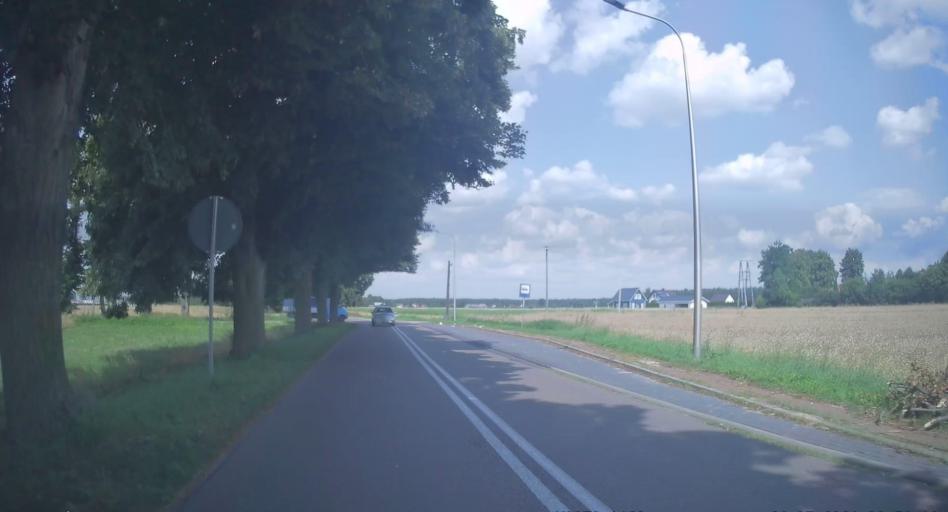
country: PL
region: Lodz Voivodeship
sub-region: Powiat tomaszowski
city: Lubochnia
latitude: 51.5684
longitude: 20.1060
